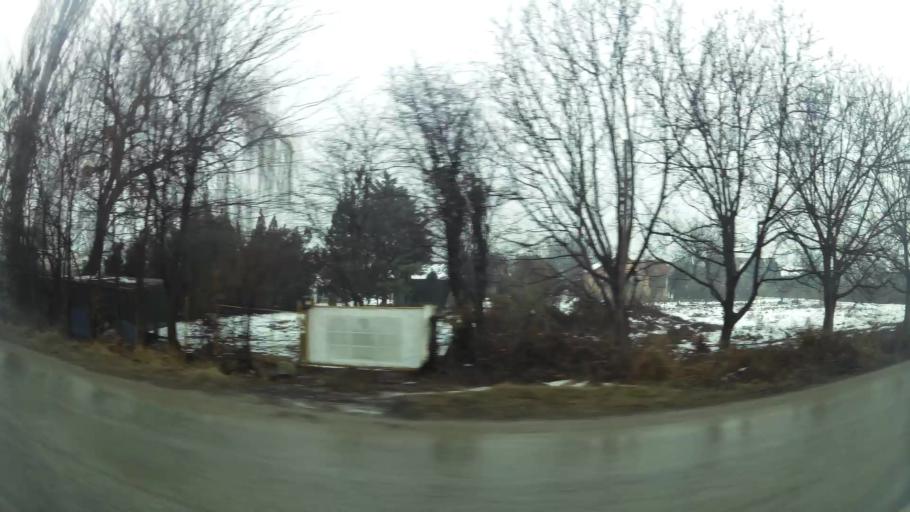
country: MK
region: Ilinden
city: Idrizovo
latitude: 41.9528
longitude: 21.5808
